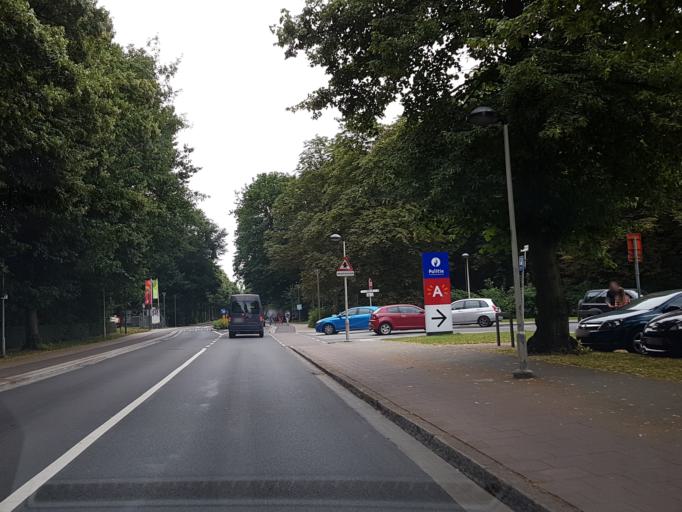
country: BE
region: Flanders
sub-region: Provincie Antwerpen
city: Borsbeek
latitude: 51.2185
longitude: 4.4608
